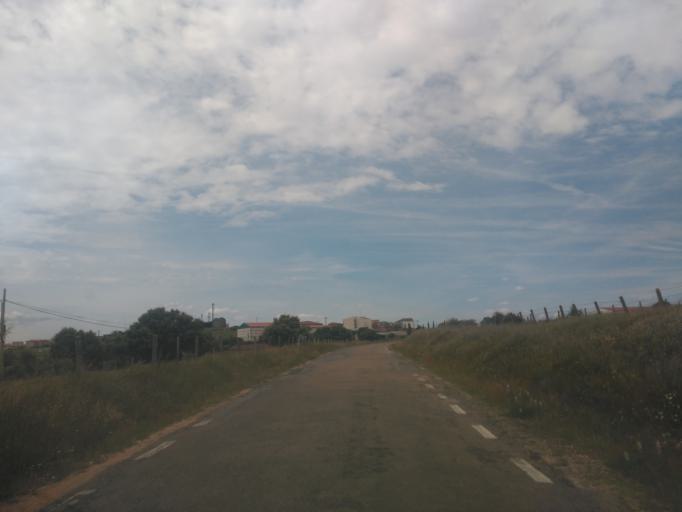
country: ES
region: Castille and Leon
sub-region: Provincia de Salamanca
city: Guijuelo
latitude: 40.5478
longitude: -5.6653
